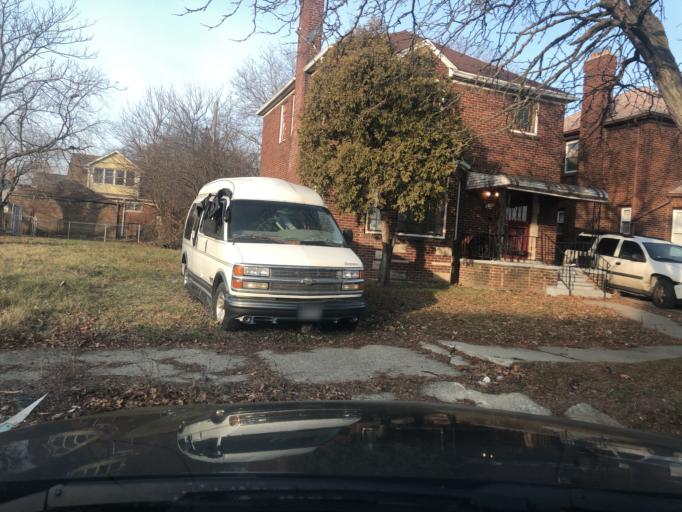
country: US
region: Michigan
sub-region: Wayne County
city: Highland Park
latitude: 42.4042
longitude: -83.1295
